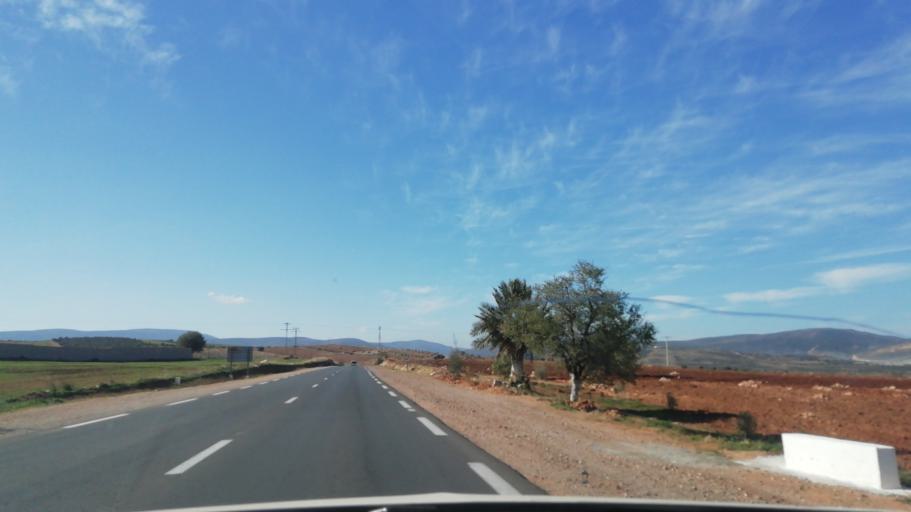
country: DZ
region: Tlemcen
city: Ouled Mimoun
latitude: 34.8775
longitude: -1.1074
